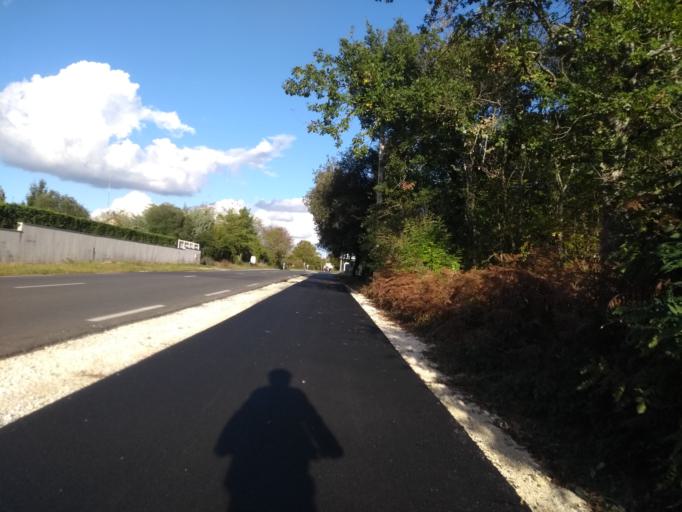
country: FR
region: Aquitaine
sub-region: Departement de la Gironde
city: Cestas
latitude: 44.7307
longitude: -0.6683
